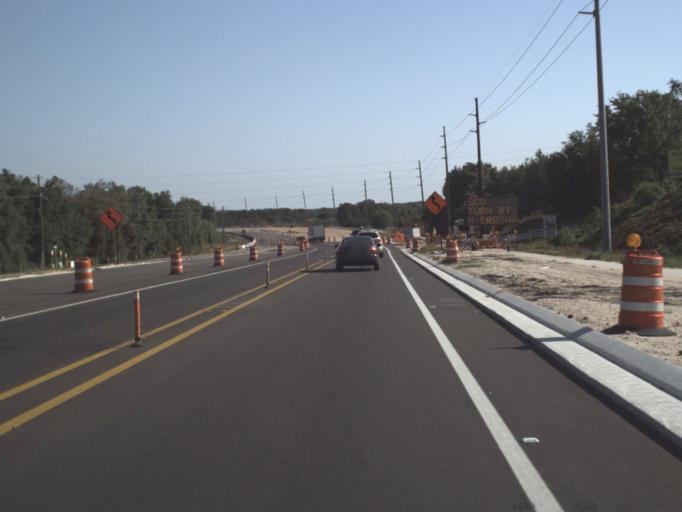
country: US
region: Florida
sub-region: Lake County
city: Clermont
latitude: 28.4698
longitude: -81.7176
